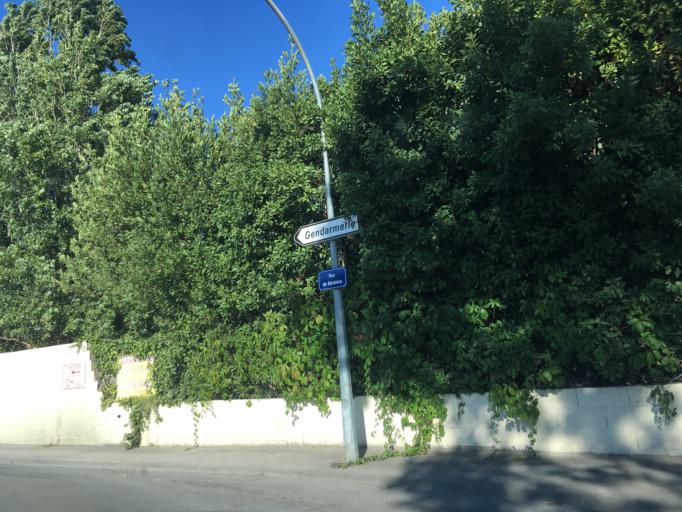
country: FR
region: Languedoc-Roussillon
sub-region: Departement du Gard
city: Aigues-Mortes
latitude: 43.5649
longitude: 4.1974
